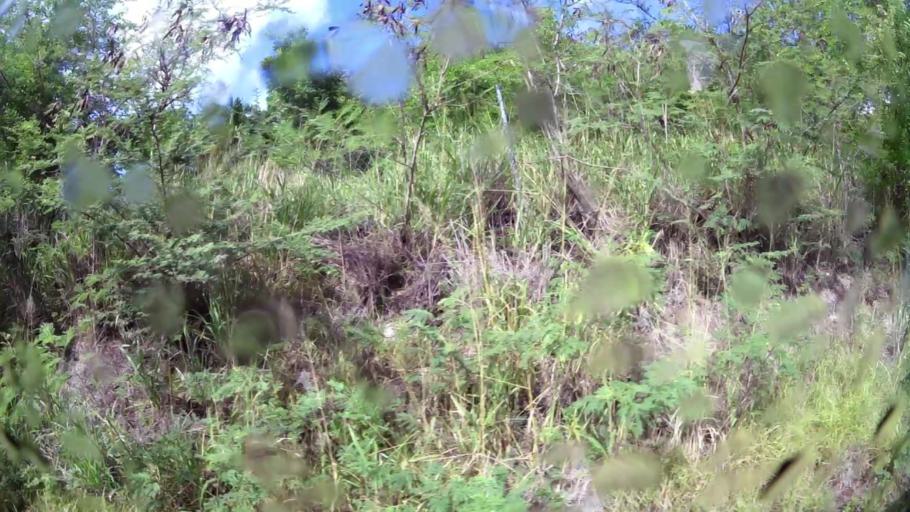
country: MS
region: Saint Peter
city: Saint Peters
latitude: 16.7455
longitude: -62.2297
